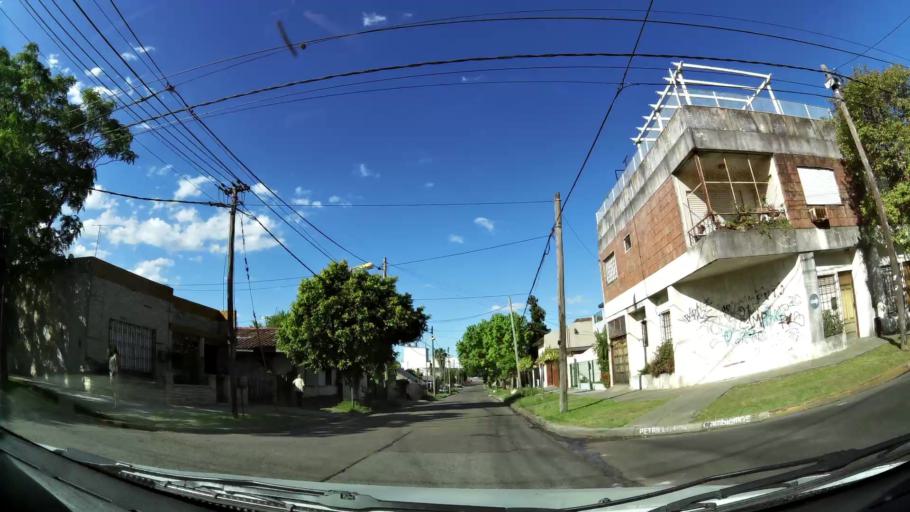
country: AR
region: Buenos Aires
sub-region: Partido de General San Martin
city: General San Martin
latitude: -34.5369
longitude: -58.5642
